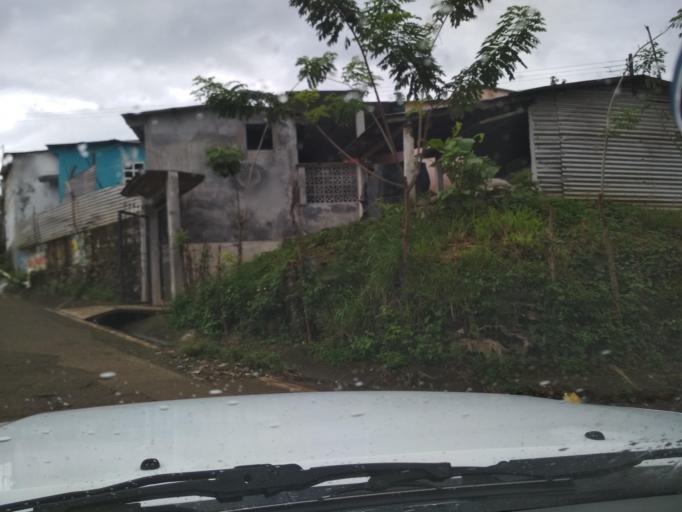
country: MX
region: Veracruz
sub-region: San Andres Tuxtla
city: San Isidro Xoteapan (San Isidro Texcaltitan)
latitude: 18.4673
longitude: -95.2382
